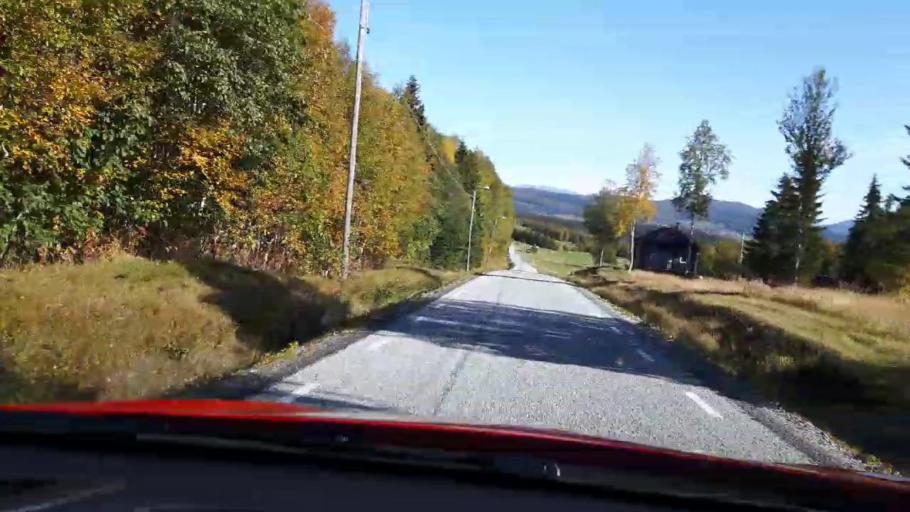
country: NO
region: Nord-Trondelag
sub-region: Royrvik
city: Royrvik
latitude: 64.7292
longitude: 13.9435
